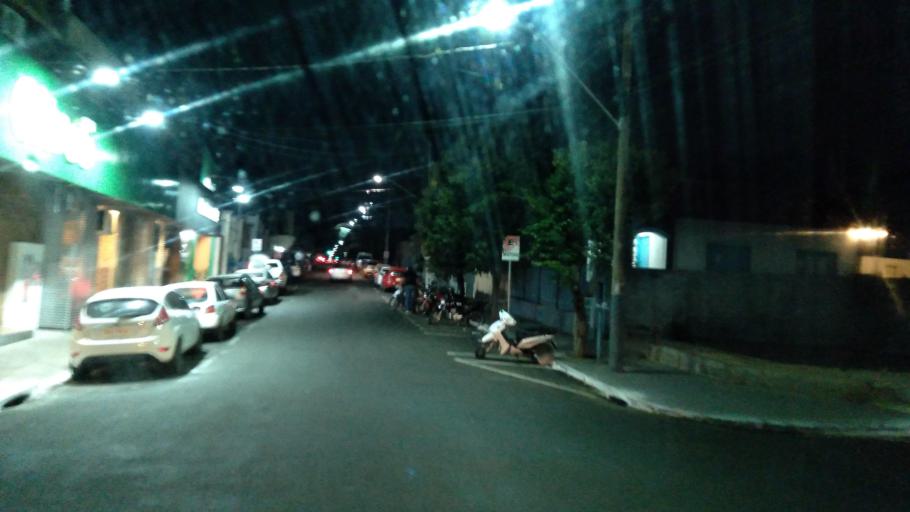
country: BR
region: Goias
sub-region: Mineiros
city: Mineiros
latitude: -17.5655
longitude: -52.5523
